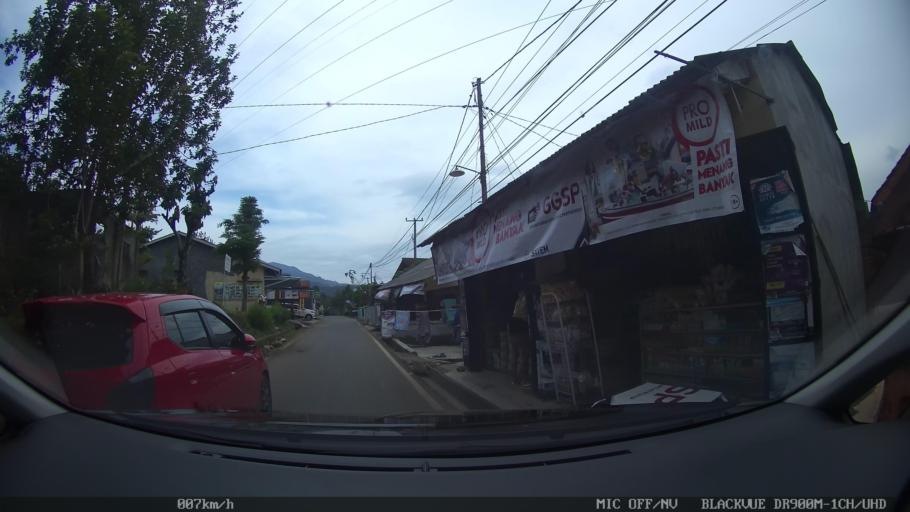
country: ID
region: Lampung
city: Kedaton
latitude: -5.3883
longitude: 105.2015
